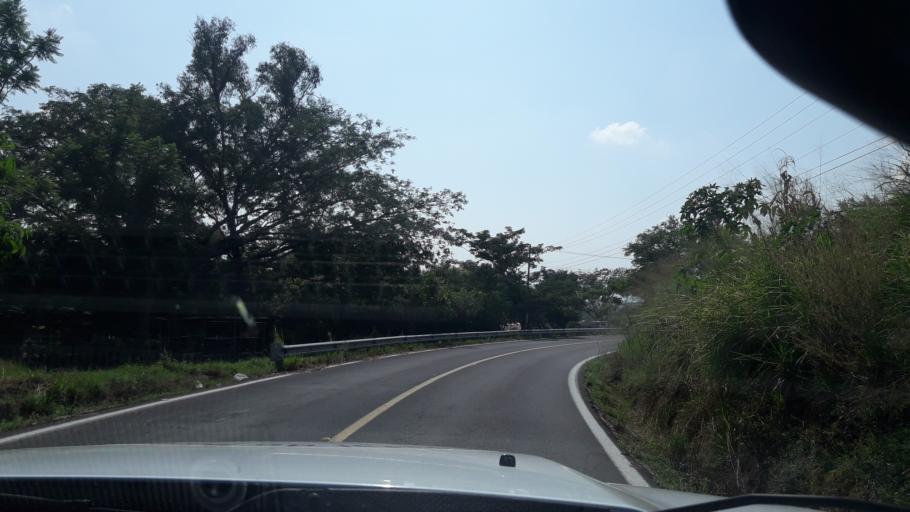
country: MX
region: Colima
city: Comala
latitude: 19.3319
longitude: -103.7487
